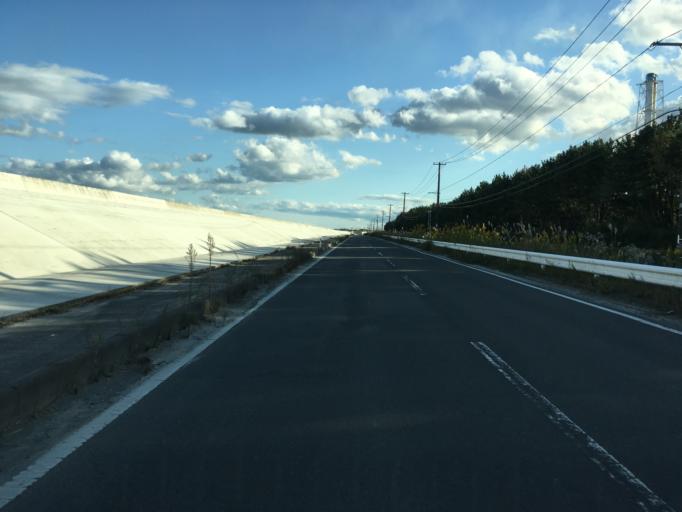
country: JP
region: Miyagi
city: Marumori
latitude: 37.8484
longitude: 140.9477
